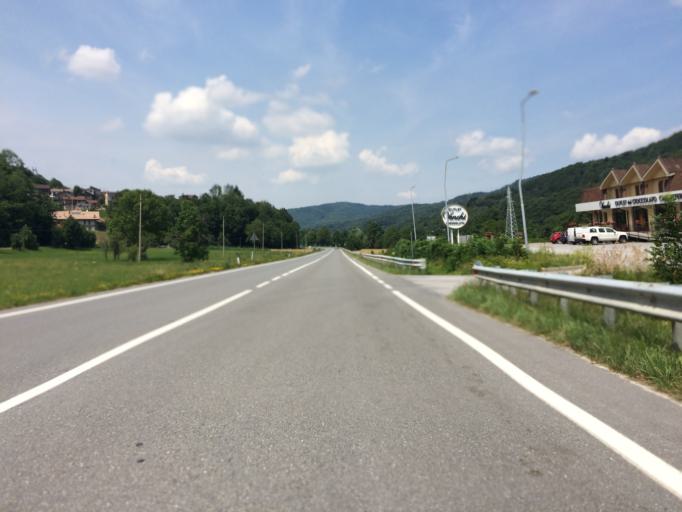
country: IT
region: Piedmont
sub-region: Provincia di Cuneo
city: Robilante
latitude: 44.2702
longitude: 7.5190
